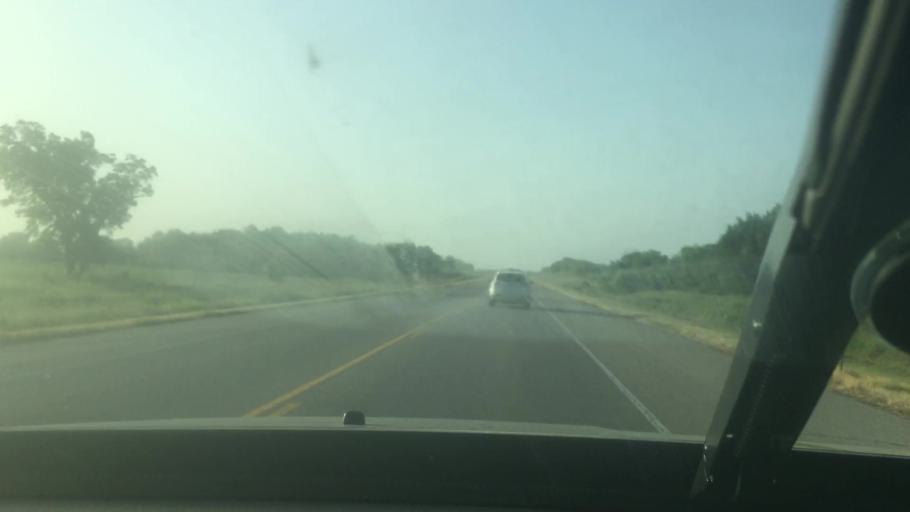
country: US
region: Oklahoma
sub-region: Pontotoc County
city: Ada
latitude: 34.7173
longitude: -96.6247
